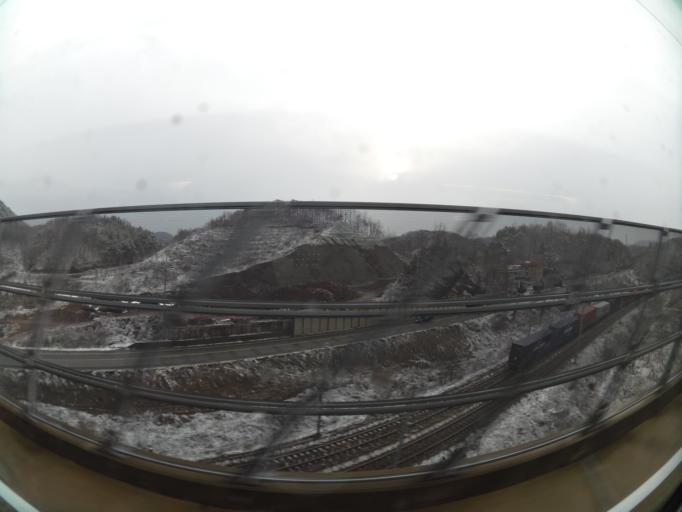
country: KR
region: Chungcheongbuk-do
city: Yong-dong
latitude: 36.1669
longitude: 127.8104
